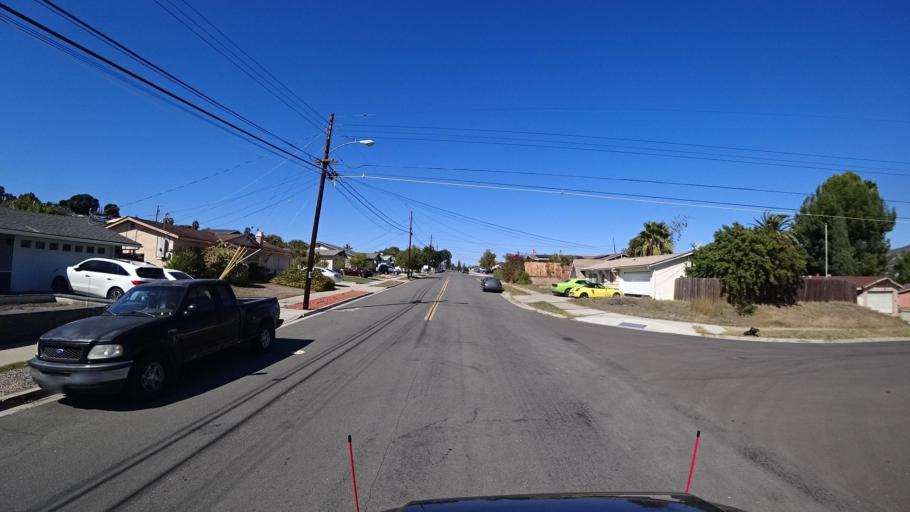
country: US
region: California
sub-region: San Diego County
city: La Presa
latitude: 32.7053
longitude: -117.0174
